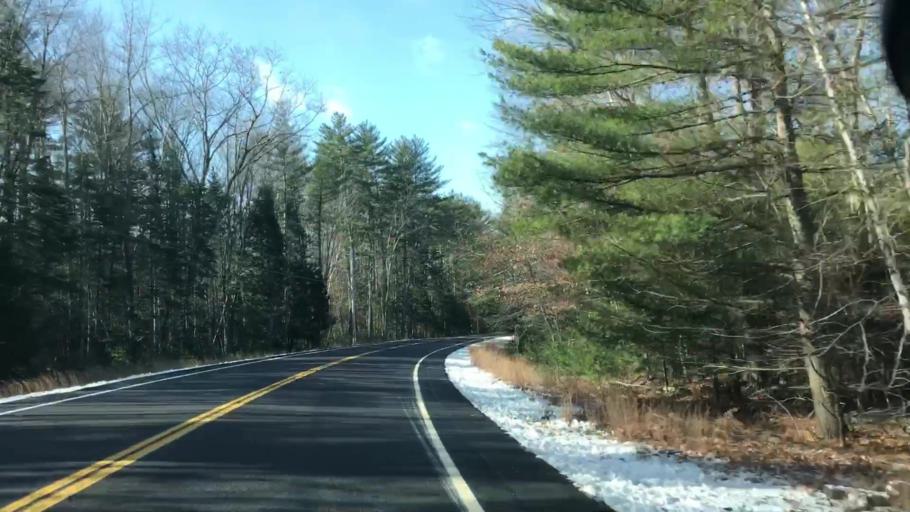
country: US
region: Maine
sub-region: Oxford County
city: Porter
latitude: 43.7879
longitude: -70.9677
